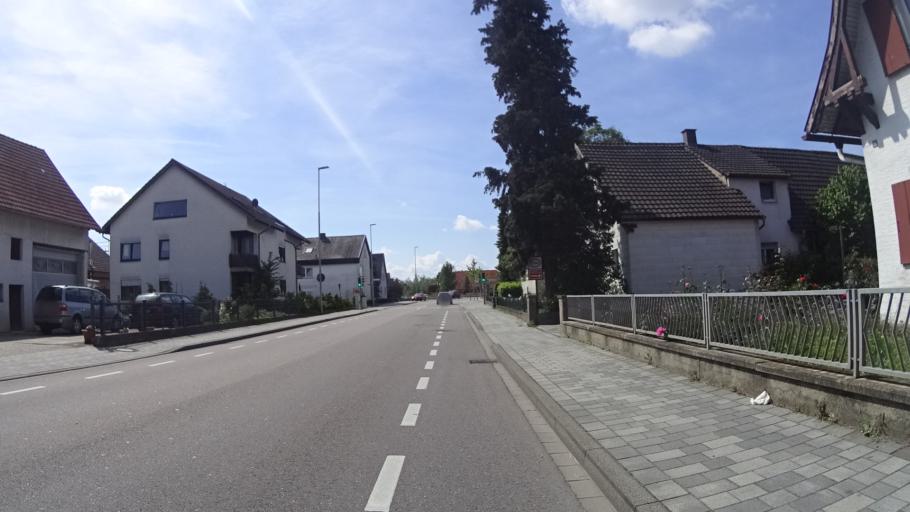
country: DE
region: Baden-Wuerttemberg
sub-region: Freiburg Region
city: Willstatt
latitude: 48.5038
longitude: 7.8226
